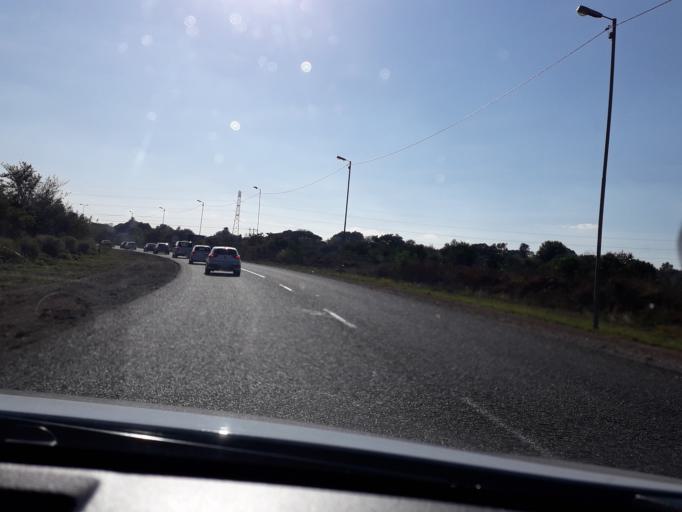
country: ZA
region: Gauteng
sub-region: City of Tshwane Metropolitan Municipality
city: Centurion
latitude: -25.8222
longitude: 28.1910
